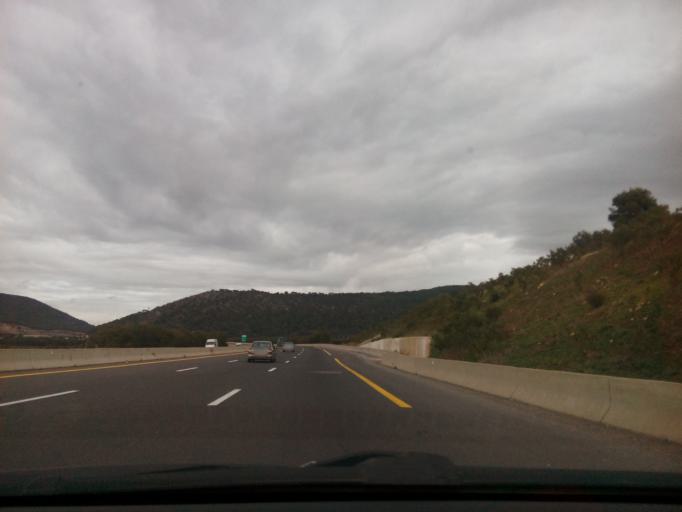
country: DZ
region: Sidi Bel Abbes
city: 'Ain el Berd
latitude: 35.3659
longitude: -0.5028
